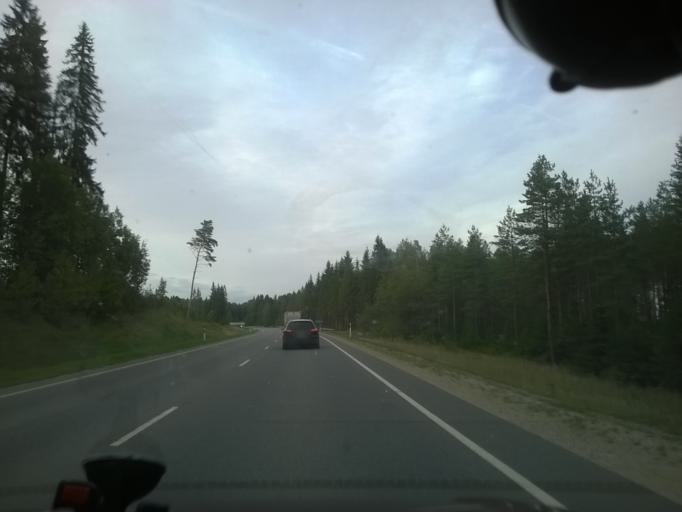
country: EE
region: Tartu
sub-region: UElenurme vald
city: Ulenurme
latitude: 58.0977
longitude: 26.7397
